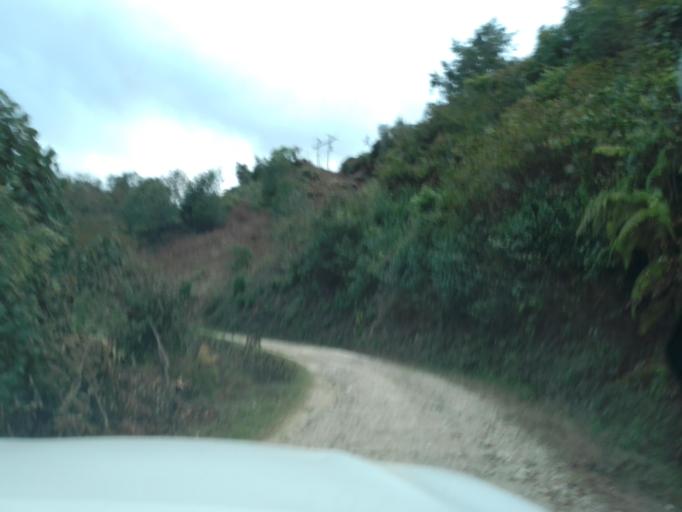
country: MX
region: Chiapas
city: Motozintla de Mendoza
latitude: 15.2110
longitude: -92.2260
